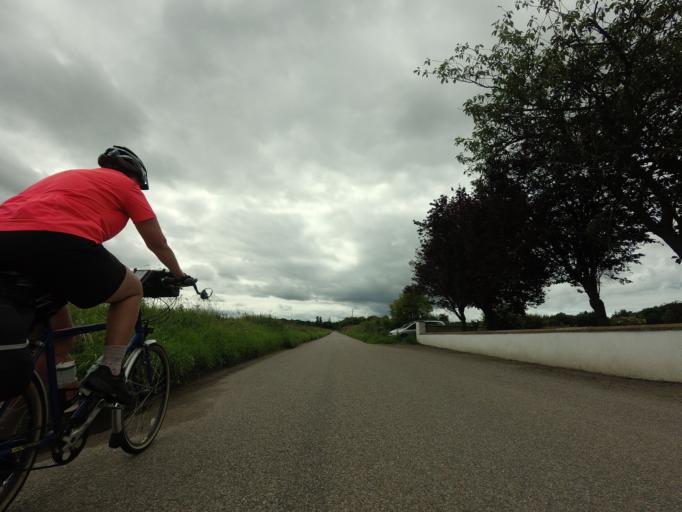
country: GB
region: Scotland
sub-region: Moray
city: Forres
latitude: 57.5996
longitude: -3.6968
